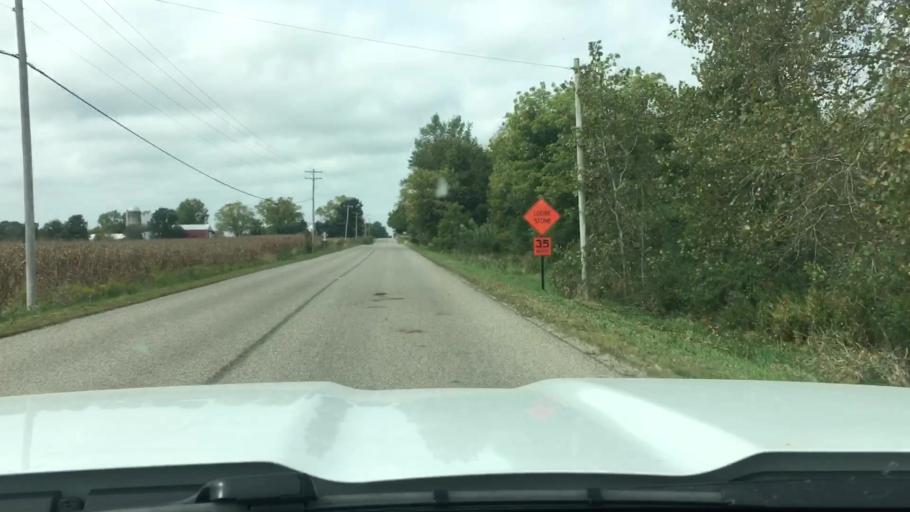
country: US
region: Michigan
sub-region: Eaton County
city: Potterville
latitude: 42.6256
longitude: -84.7064
